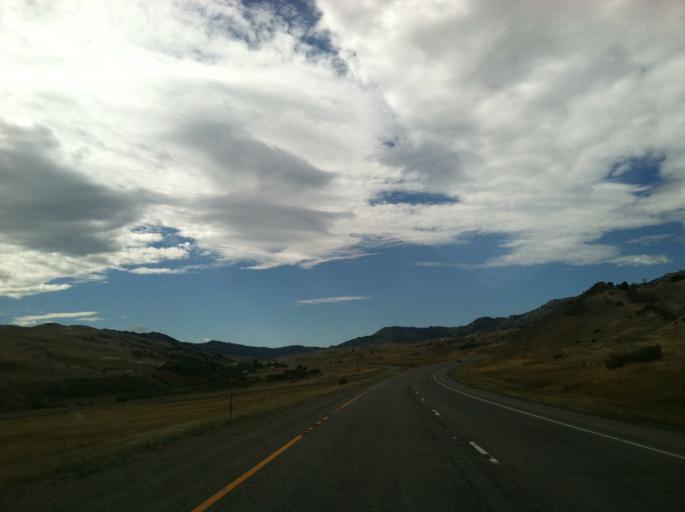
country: US
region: Montana
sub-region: Park County
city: Livingston
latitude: 45.6632
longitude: -110.6773
